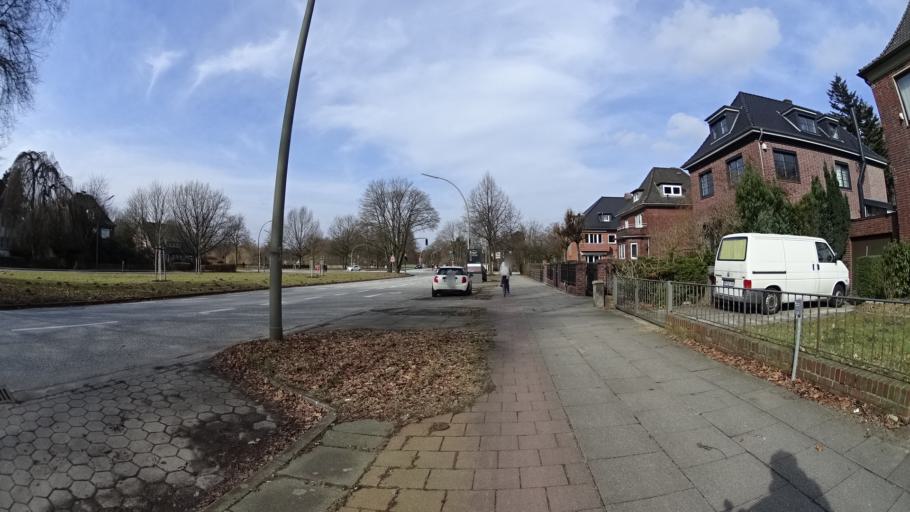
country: DE
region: Hamburg
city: Alsterdorf
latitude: 53.6110
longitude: 10.0111
